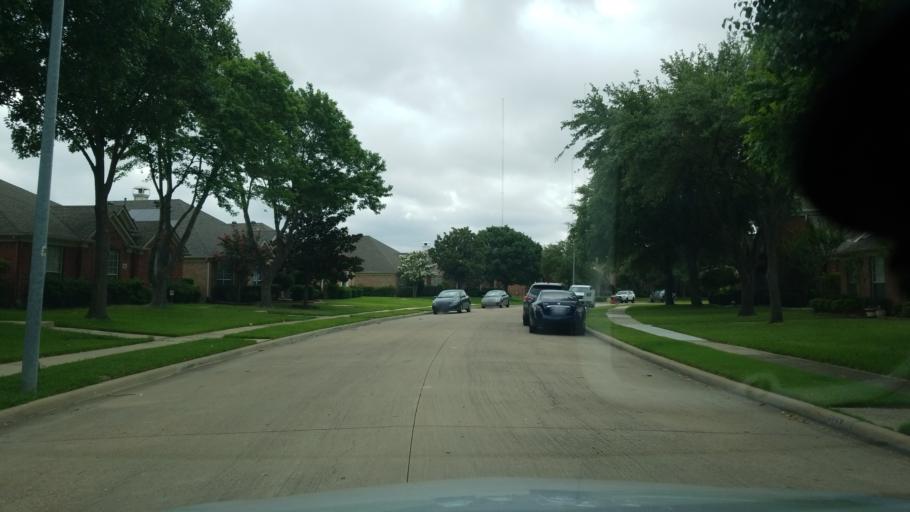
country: US
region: Texas
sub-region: Dallas County
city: Farmers Branch
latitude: 32.9469
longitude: -96.9453
